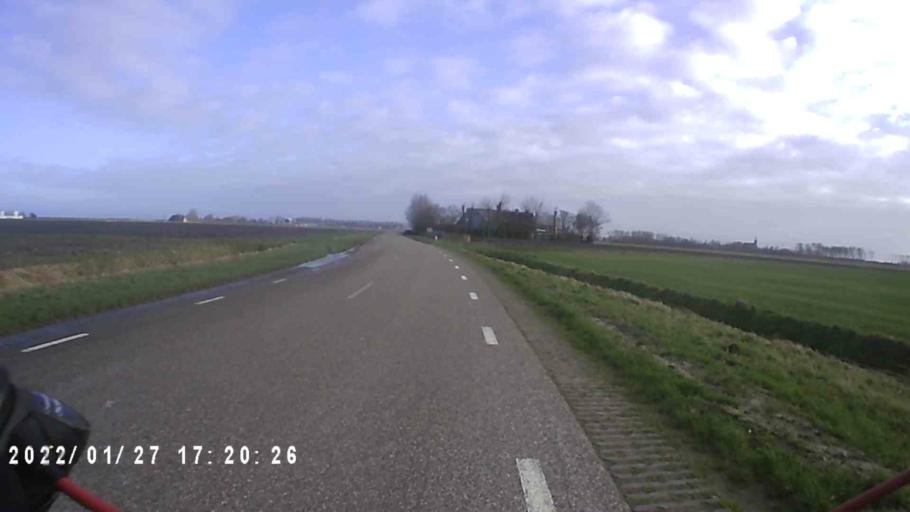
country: NL
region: Friesland
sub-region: Gemeente Dongeradeel
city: Anjum
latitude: 53.3838
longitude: 6.1142
